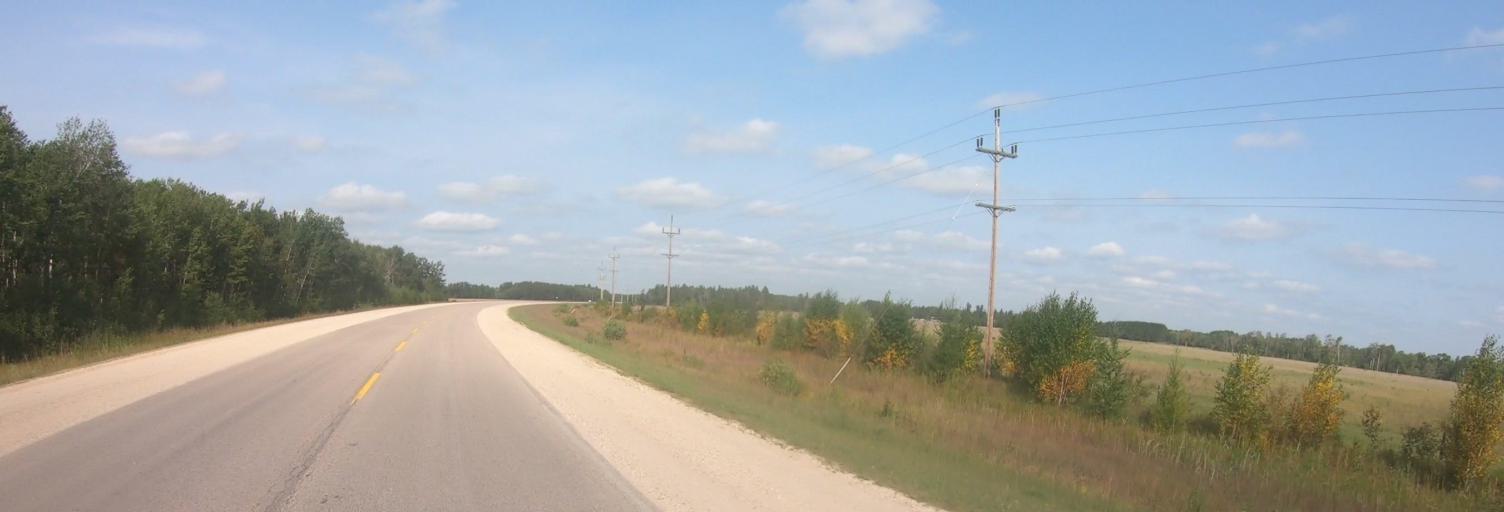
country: CA
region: Manitoba
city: La Broquerie
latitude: 49.1783
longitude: -96.2288
